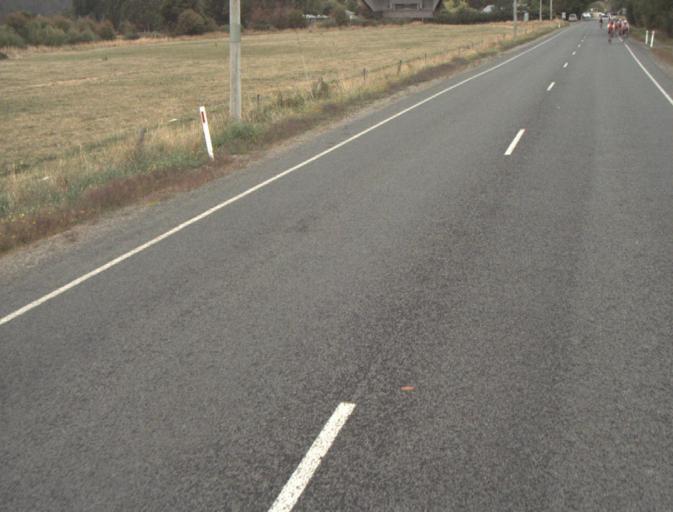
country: AU
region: Tasmania
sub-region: Launceston
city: Mayfield
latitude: -41.2460
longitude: 147.2173
